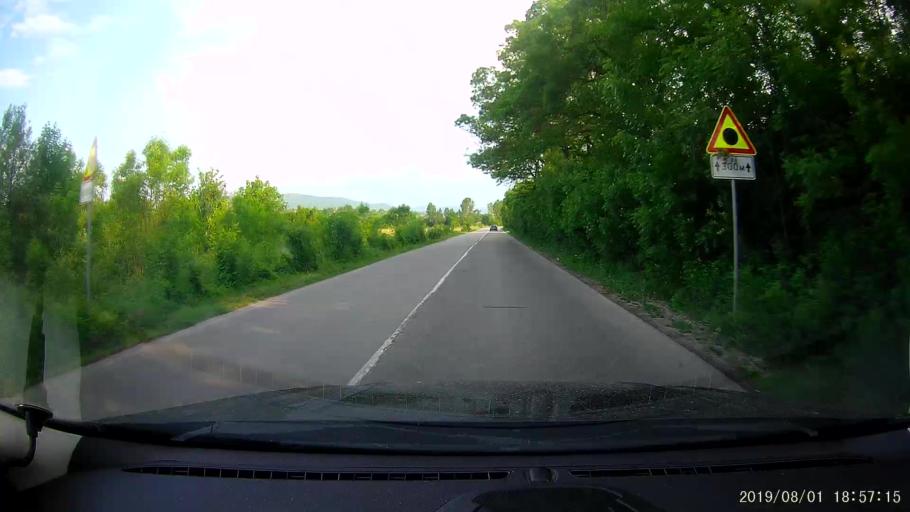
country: BG
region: Shumen
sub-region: Obshtina Smyadovo
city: Smyadovo
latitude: 43.1505
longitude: 27.0218
